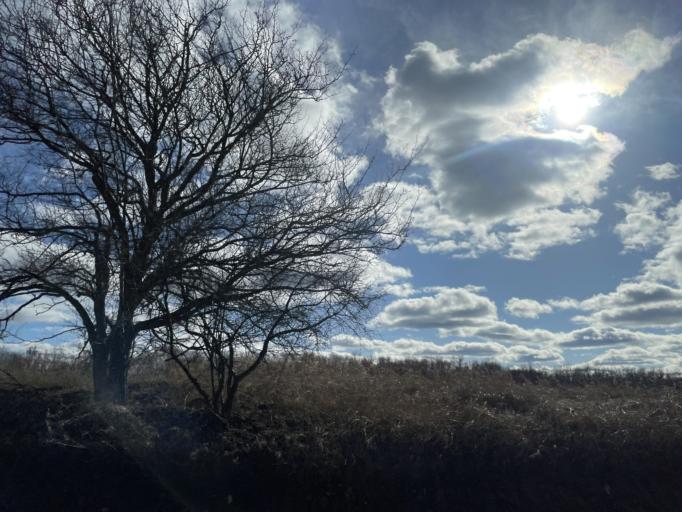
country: CA
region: Ontario
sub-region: Wellington County
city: Guelph
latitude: 43.5187
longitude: -80.2872
